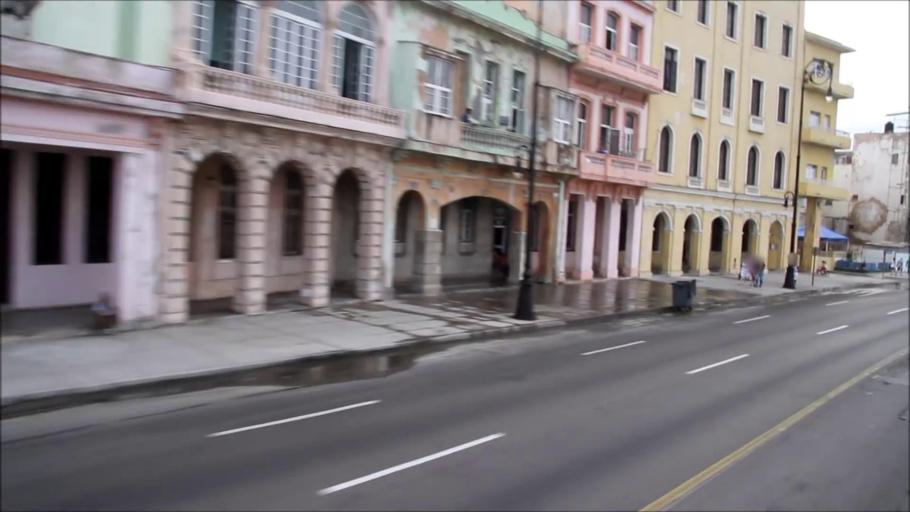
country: CU
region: La Habana
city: Centro Habana
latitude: 23.1417
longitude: -82.3687
